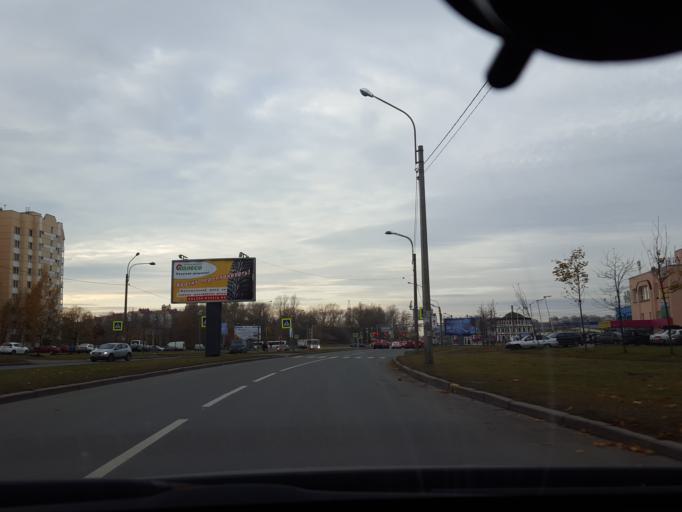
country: RU
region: St.-Petersburg
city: Kolomyagi
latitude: 60.0229
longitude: 30.2856
